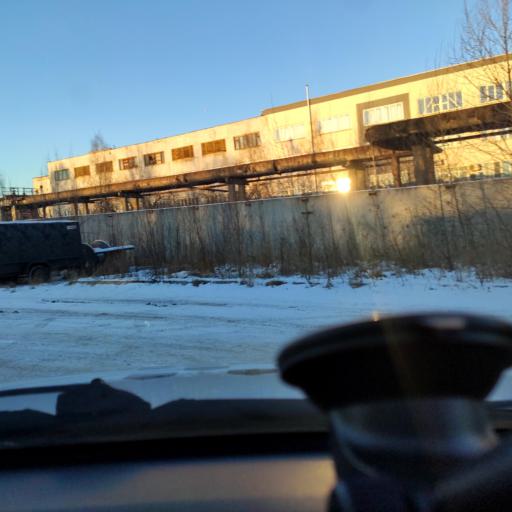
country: RU
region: Perm
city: Perm
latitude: 58.0408
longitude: 56.3107
